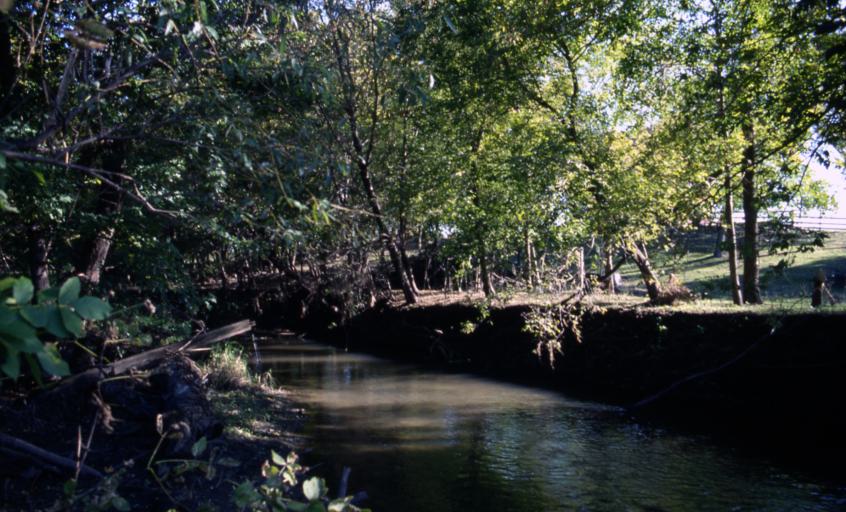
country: US
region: Minnesota
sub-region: Wabasha County
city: Elgin
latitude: 44.1235
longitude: -92.2419
